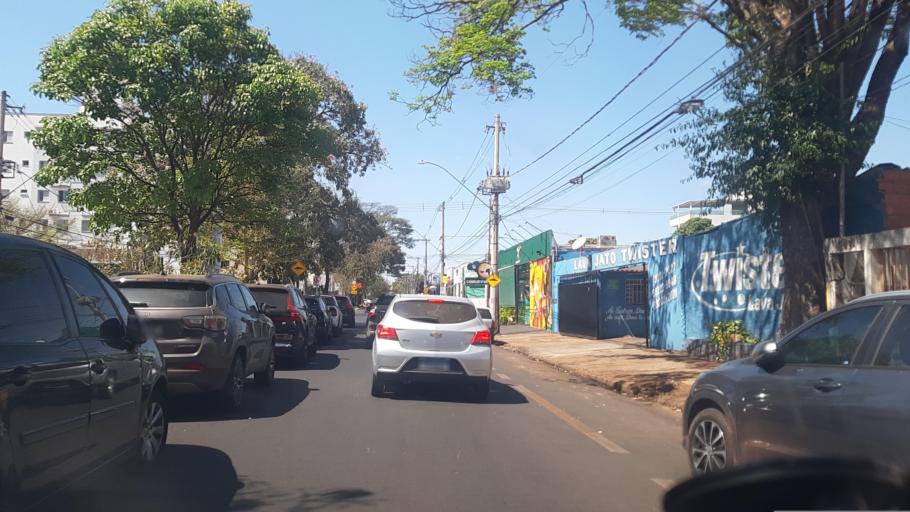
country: BR
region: Minas Gerais
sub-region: Uberlandia
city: Uberlandia
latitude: -18.9333
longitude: -48.2890
